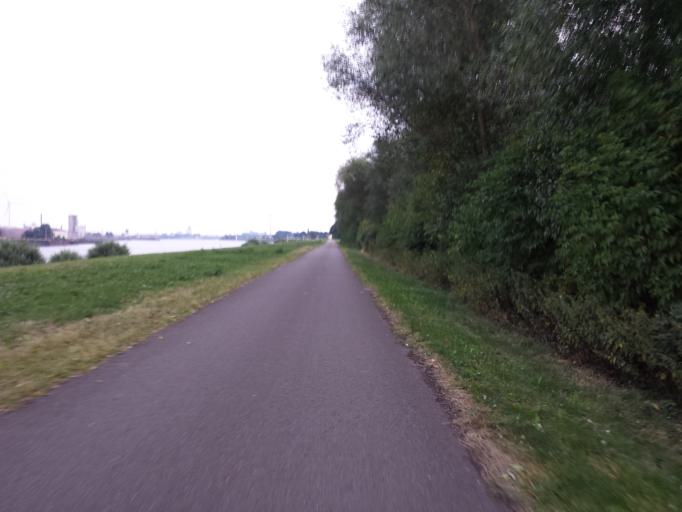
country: DE
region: Lower Saxony
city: Lemwerder
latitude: 53.1215
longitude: 8.6774
